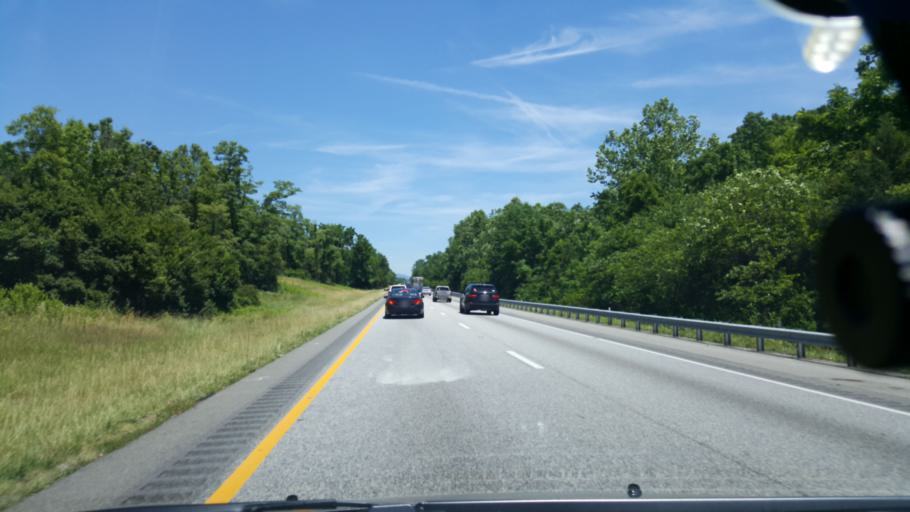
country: US
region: Virginia
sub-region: Botetourt County
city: Daleville
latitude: 37.4311
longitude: -79.8738
